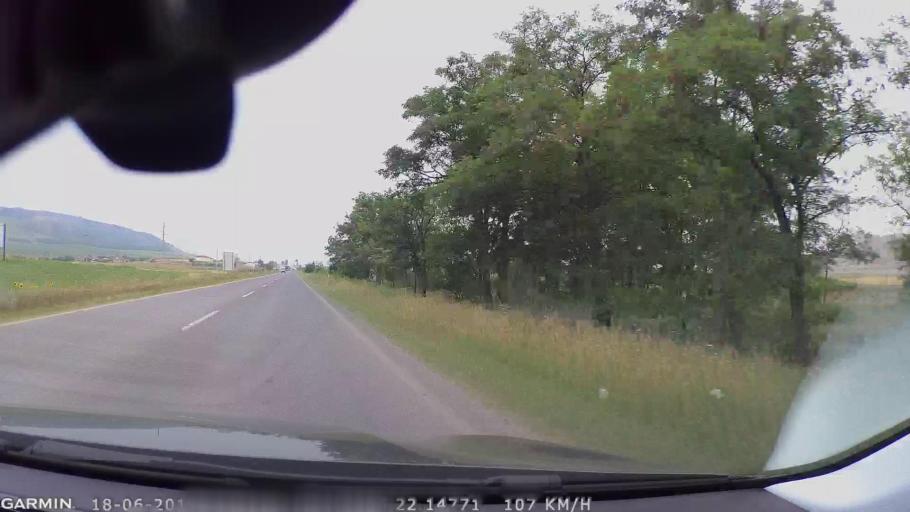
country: MK
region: Stip
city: Shtip
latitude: 41.7704
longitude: 22.1469
